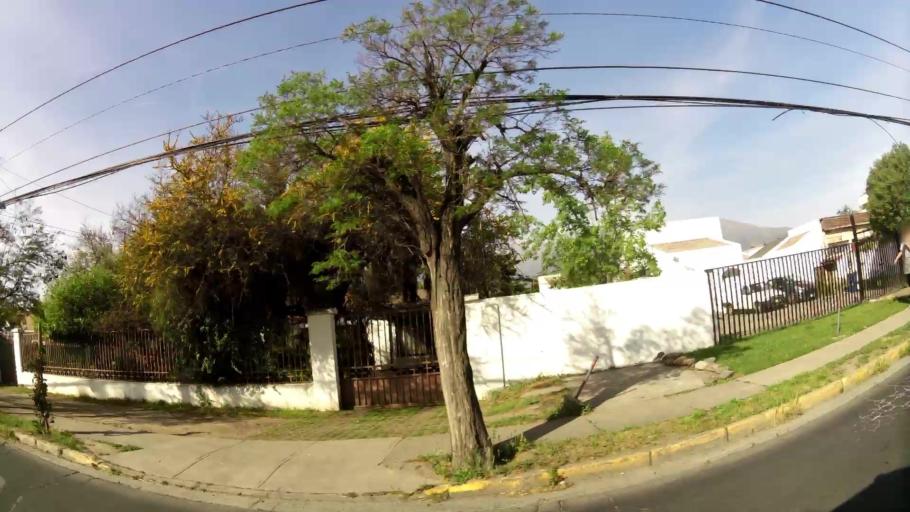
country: CL
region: Santiago Metropolitan
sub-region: Provincia de Santiago
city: La Pintana
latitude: -33.5394
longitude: -70.5833
